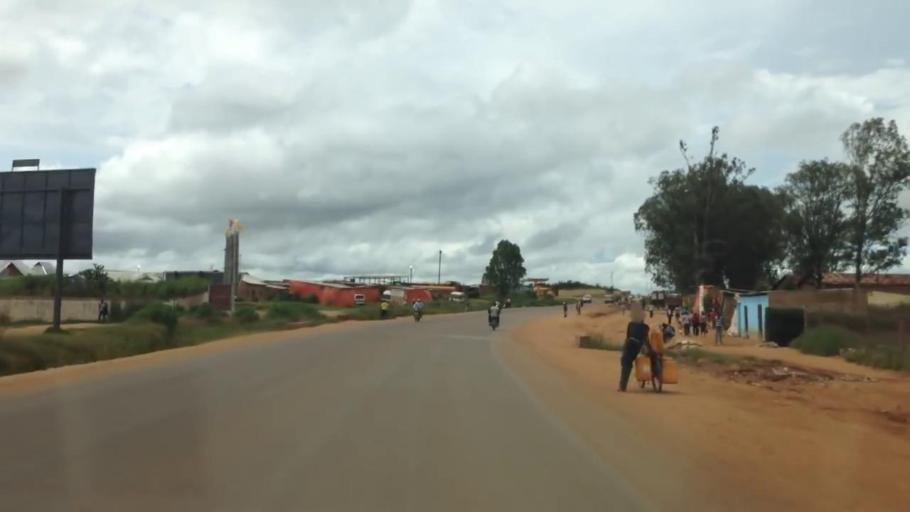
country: CD
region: Katanga
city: Kolwezi
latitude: -10.7230
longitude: 25.5079
